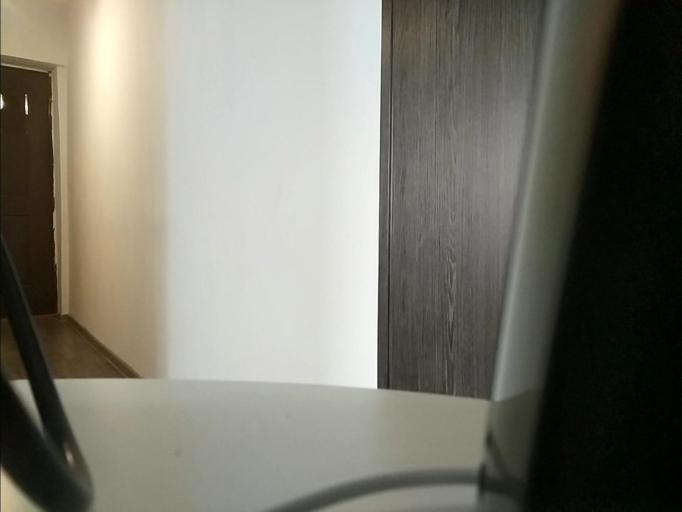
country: RU
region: Moskovskaya
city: Balashikha
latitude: 55.8077
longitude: 37.9593
